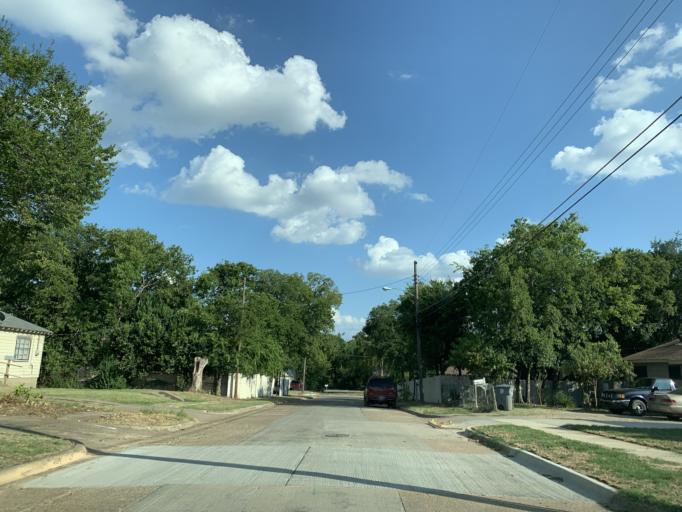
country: US
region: Texas
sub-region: Dallas County
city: Hutchins
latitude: 32.6954
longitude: -96.7817
